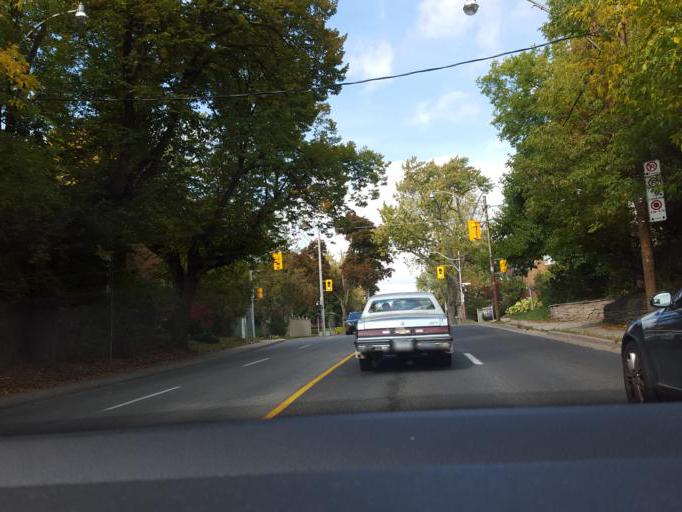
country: CA
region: Ontario
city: Toronto
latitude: 43.7219
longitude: -79.3955
